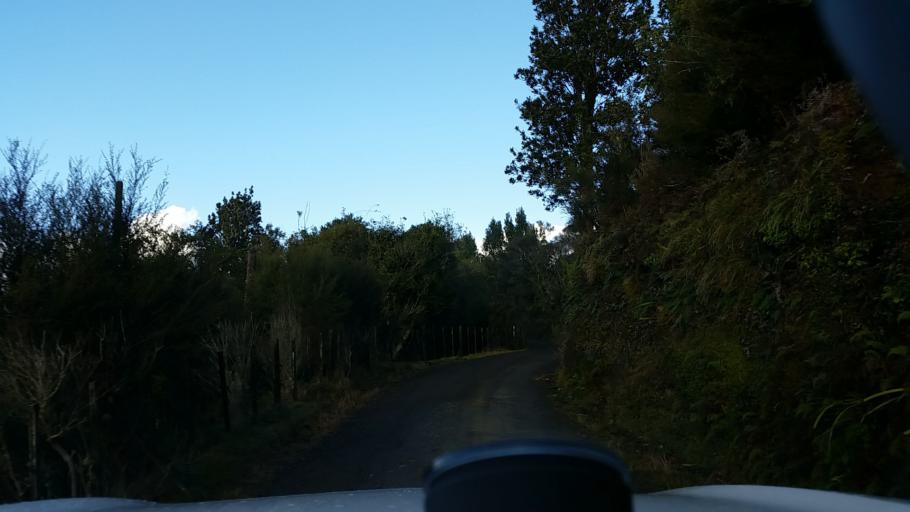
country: NZ
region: Taranaki
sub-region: South Taranaki District
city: Eltham
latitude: -39.4201
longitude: 174.5570
